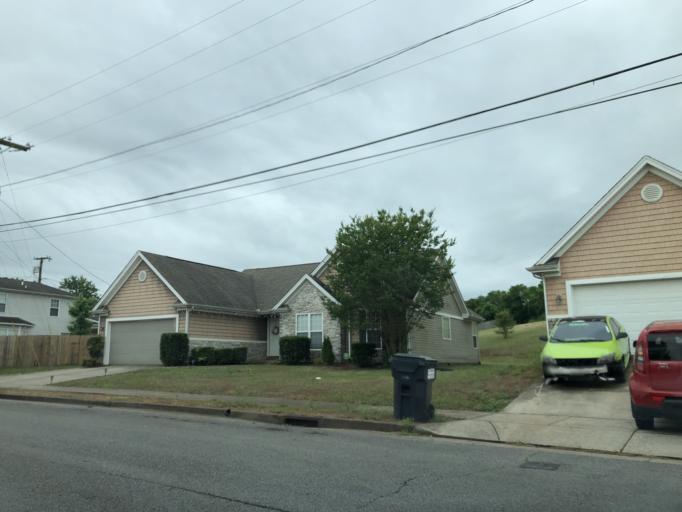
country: US
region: Tennessee
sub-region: Davidson County
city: Goodlettsville
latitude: 36.2749
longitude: -86.7691
